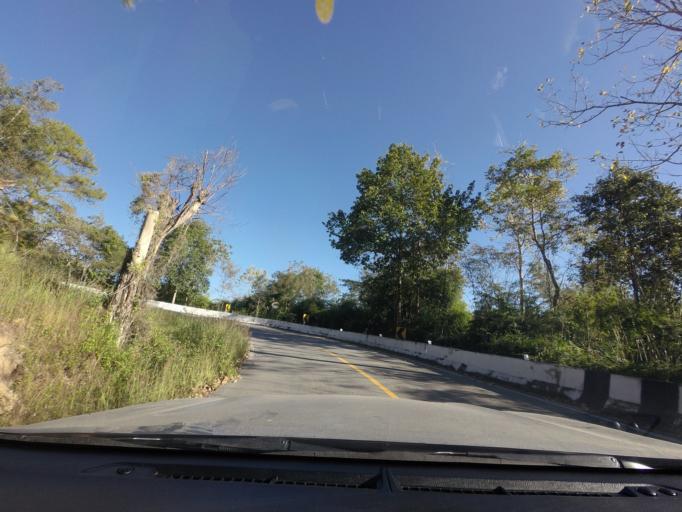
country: TH
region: Mae Hong Son
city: Mae Hi
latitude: 19.2184
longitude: 98.6725
